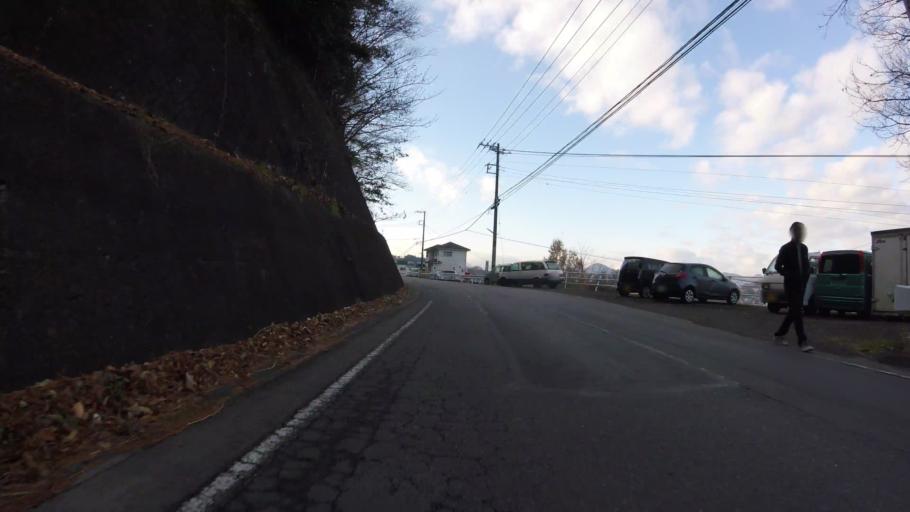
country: JP
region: Shizuoka
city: Mishima
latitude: 35.1021
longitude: 138.9643
